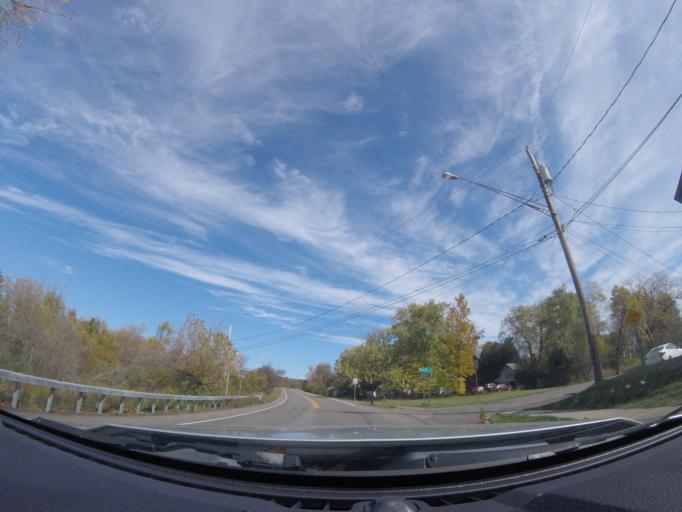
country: US
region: New York
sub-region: Tompkins County
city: Dryden
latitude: 42.5144
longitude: -76.3459
